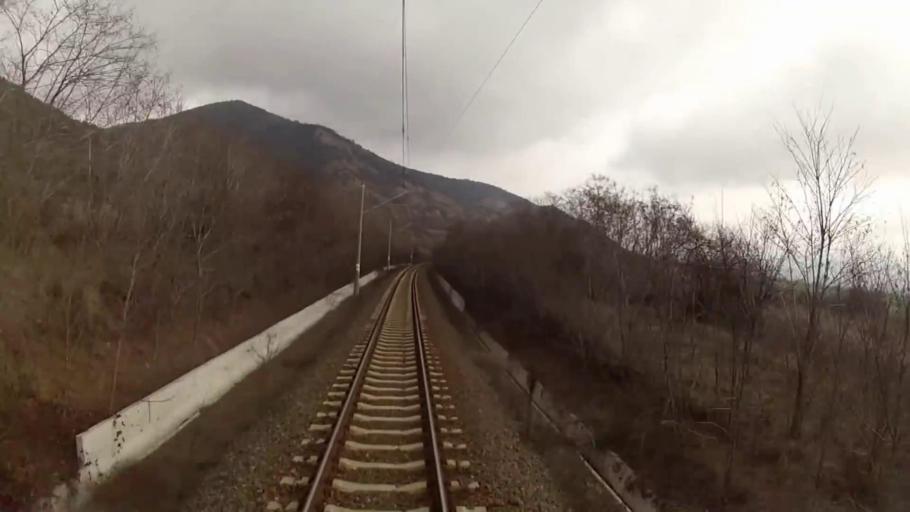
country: BG
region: Sofiya
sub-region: Obshtina Chelopech
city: Chelopech
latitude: 42.6929
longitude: 24.0460
